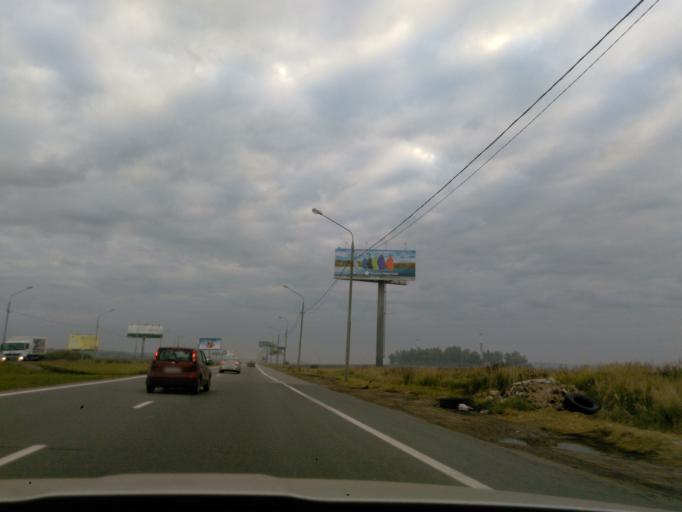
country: RU
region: Moskovskaya
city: Novopodrezkovo
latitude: 55.9565
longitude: 37.3491
